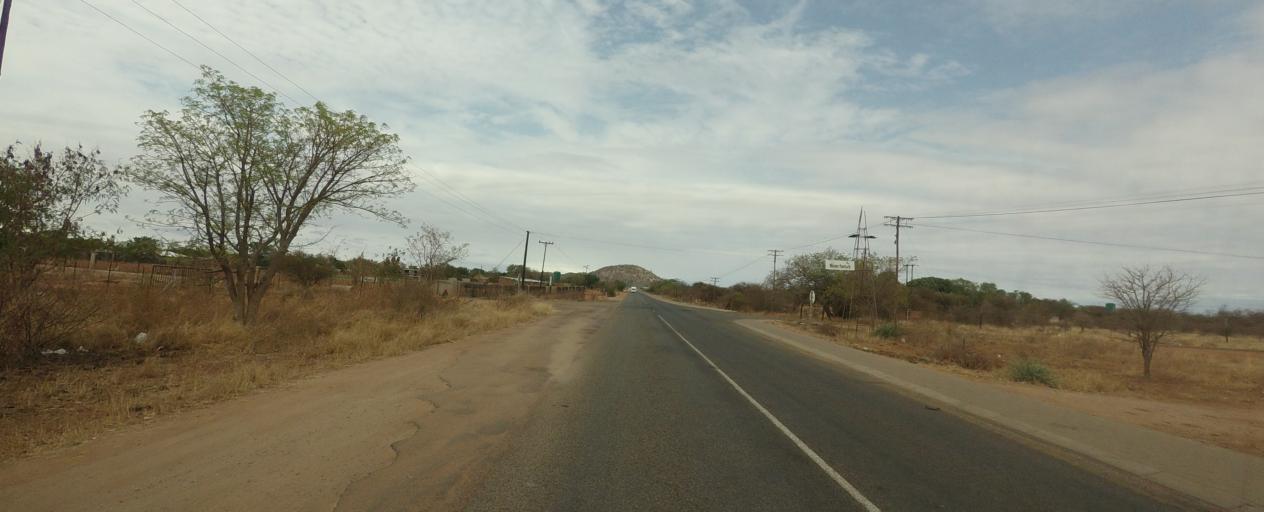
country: BW
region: Central
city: Mathathane
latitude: -22.6733
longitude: 29.1101
